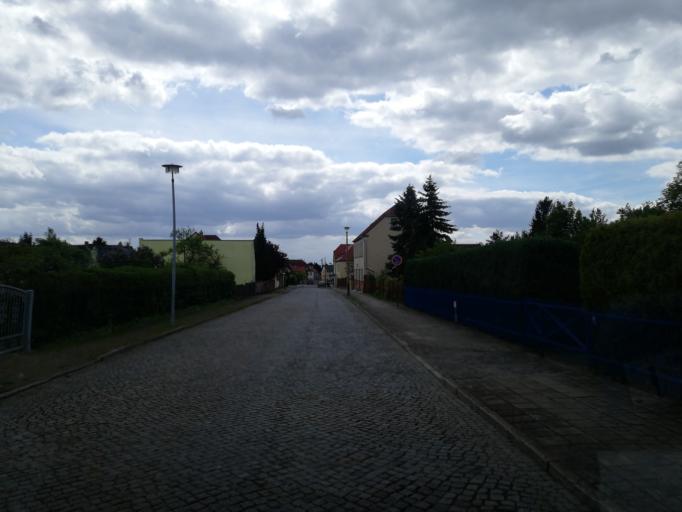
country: DE
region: Brandenburg
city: Lauchhammer
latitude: 51.4972
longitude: 13.7634
